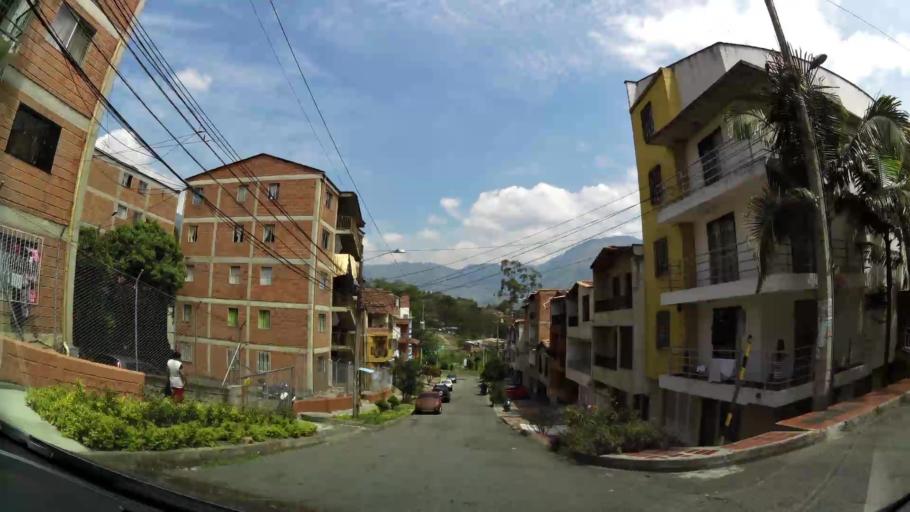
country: CO
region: Antioquia
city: Bello
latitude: 6.3197
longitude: -75.5652
